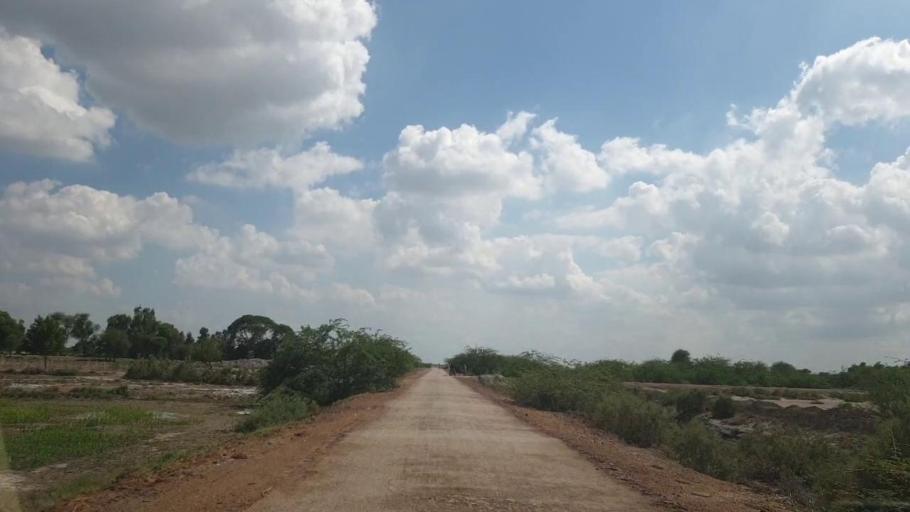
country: PK
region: Sindh
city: Pithoro
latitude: 25.5989
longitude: 69.4035
